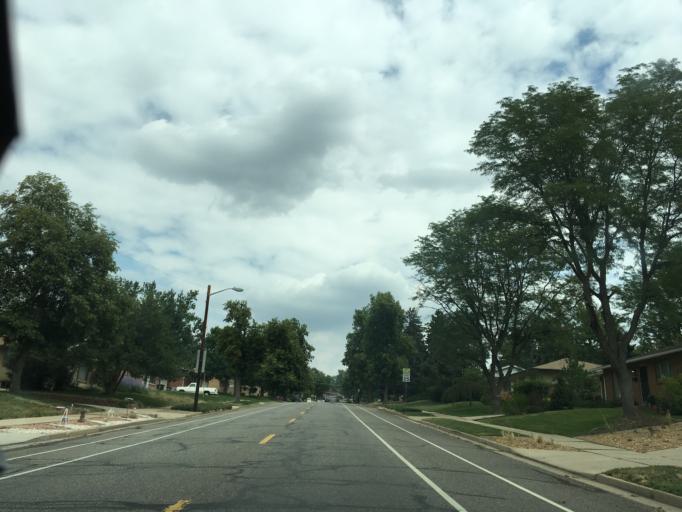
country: US
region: Colorado
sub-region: Arapahoe County
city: Sheridan
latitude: 39.6607
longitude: -105.0440
